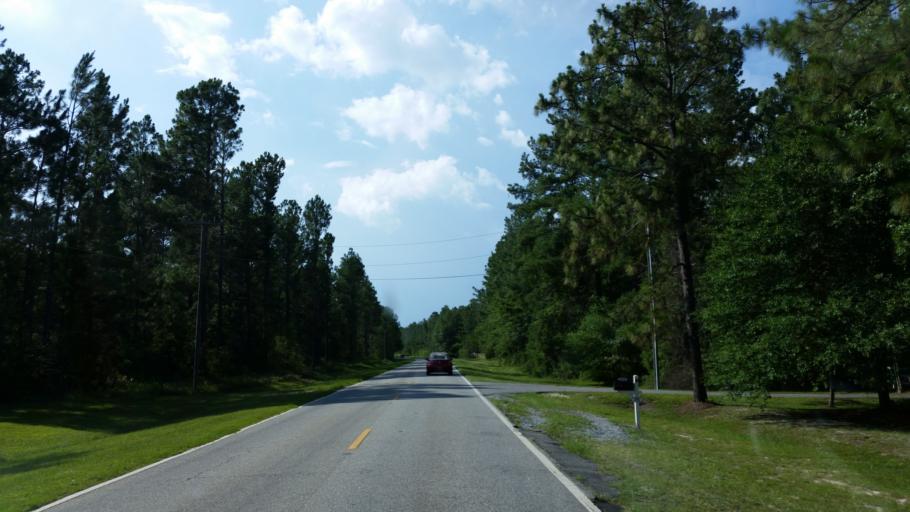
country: US
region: Georgia
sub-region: Lowndes County
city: Hahira
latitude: 30.9066
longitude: -83.3819
